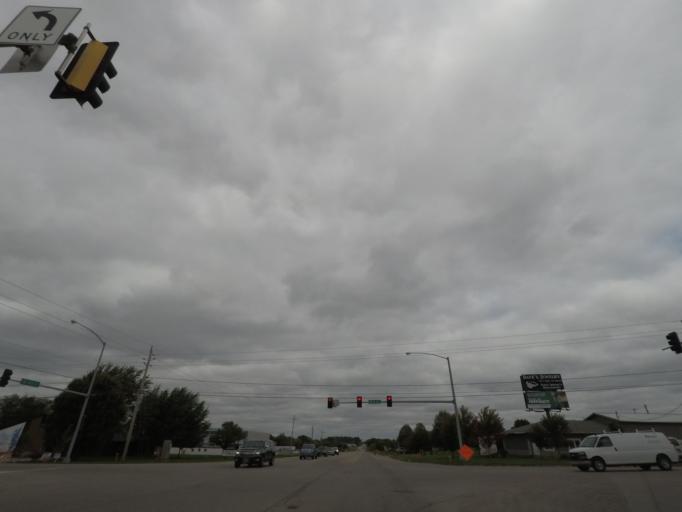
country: US
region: Iowa
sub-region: Polk County
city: Saylorville
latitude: 41.6802
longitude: -93.6006
